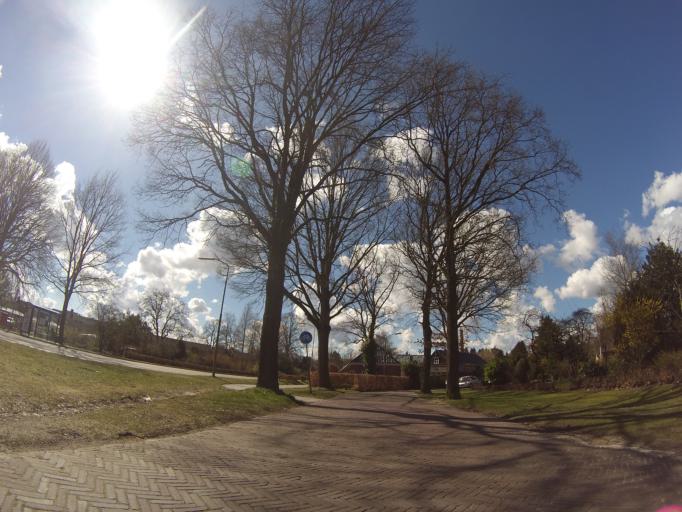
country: NL
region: Drenthe
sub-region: Gemeente Emmen
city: Emmen
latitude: 52.7751
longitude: 6.8829
